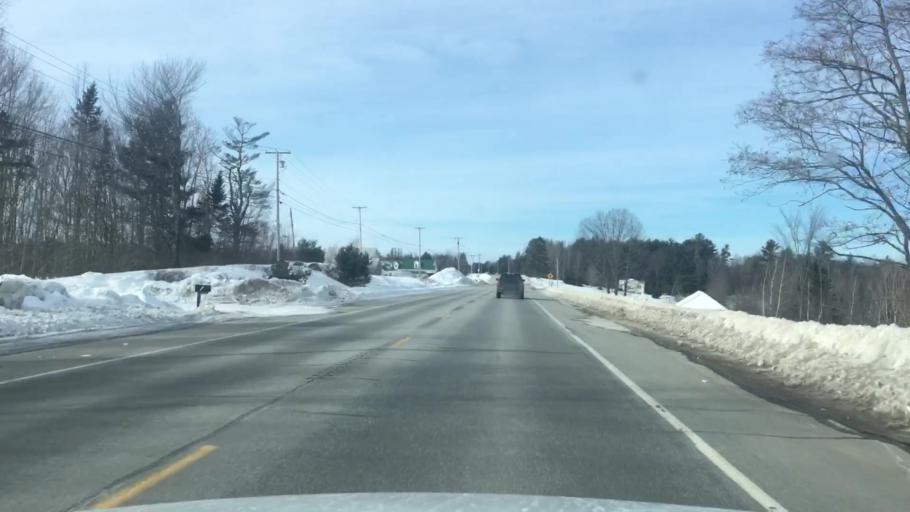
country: US
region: Maine
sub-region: Penobscot County
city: Kenduskeag
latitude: 44.9505
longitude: -68.9477
